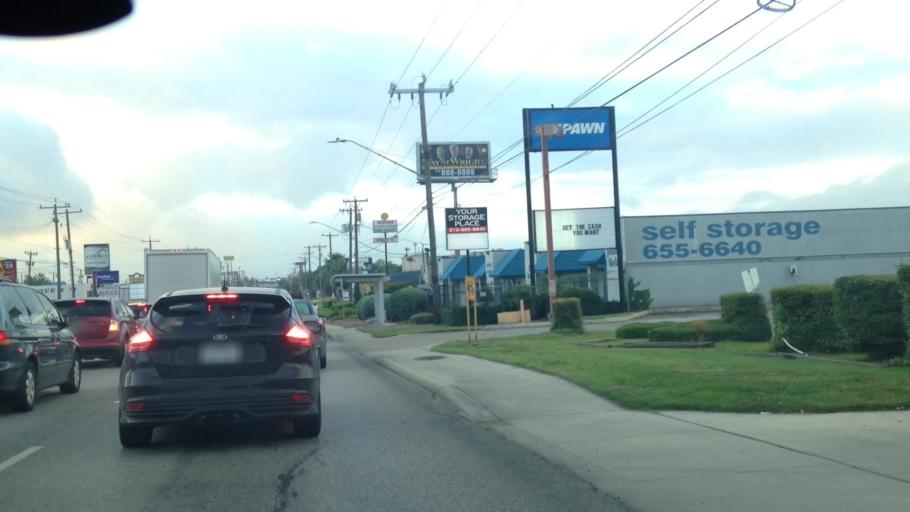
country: US
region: Texas
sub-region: Bexar County
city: Windcrest
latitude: 29.5263
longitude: -98.4111
